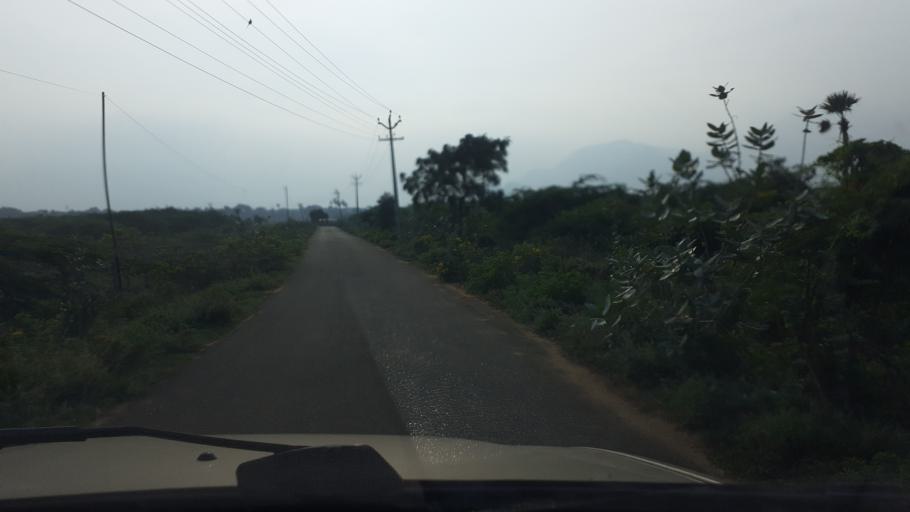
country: IN
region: Tamil Nadu
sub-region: Tirunelveli Kattabo
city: Kalakkadu
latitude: 8.4730
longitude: 77.5872
